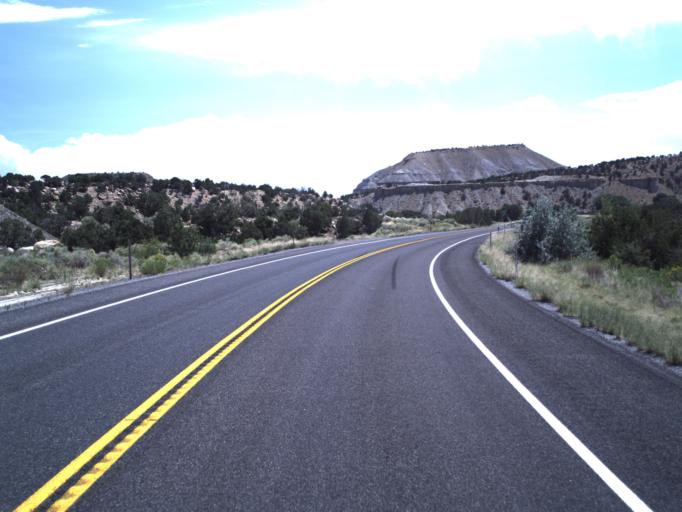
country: US
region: Utah
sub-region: Emery County
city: Huntington
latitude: 39.3661
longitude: -111.0494
